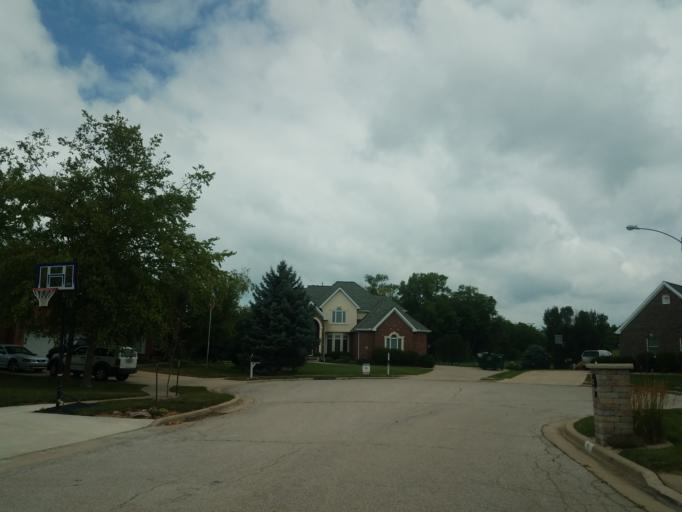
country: US
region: Illinois
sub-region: McLean County
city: Twin Grove
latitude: 40.4525
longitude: -89.0460
